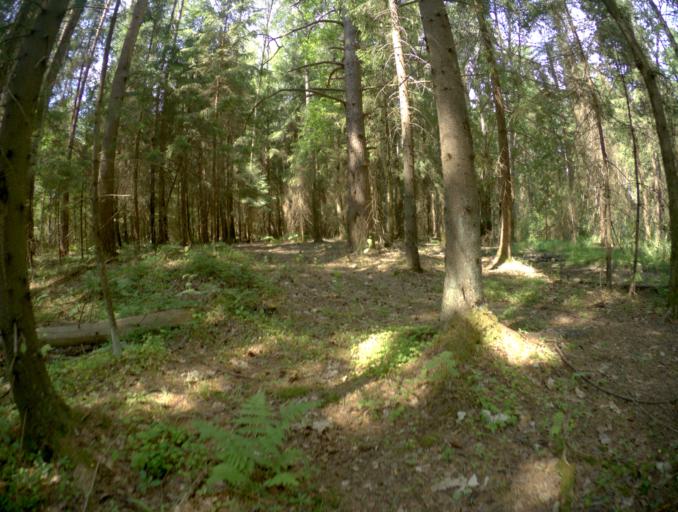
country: RU
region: Vladimir
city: Raduzhnyy
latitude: 56.0234
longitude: 40.2534
